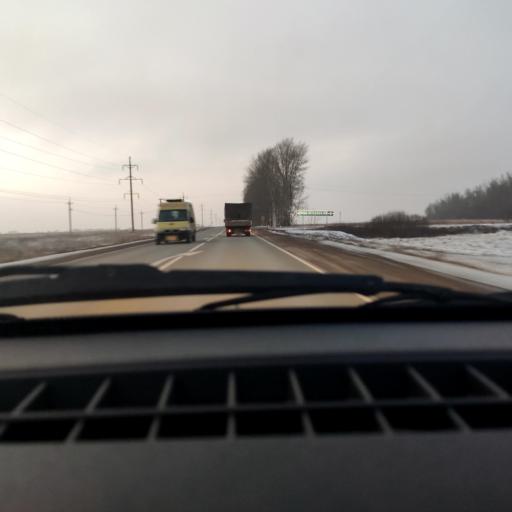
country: RU
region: Bashkortostan
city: Mikhaylovka
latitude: 54.8478
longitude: 55.7787
